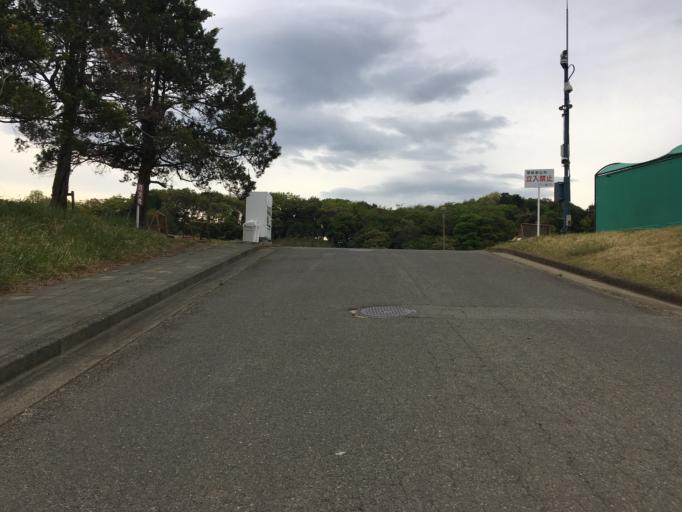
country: JP
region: Tokyo
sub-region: Machida-shi
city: Machida
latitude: 35.5695
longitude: 139.4805
